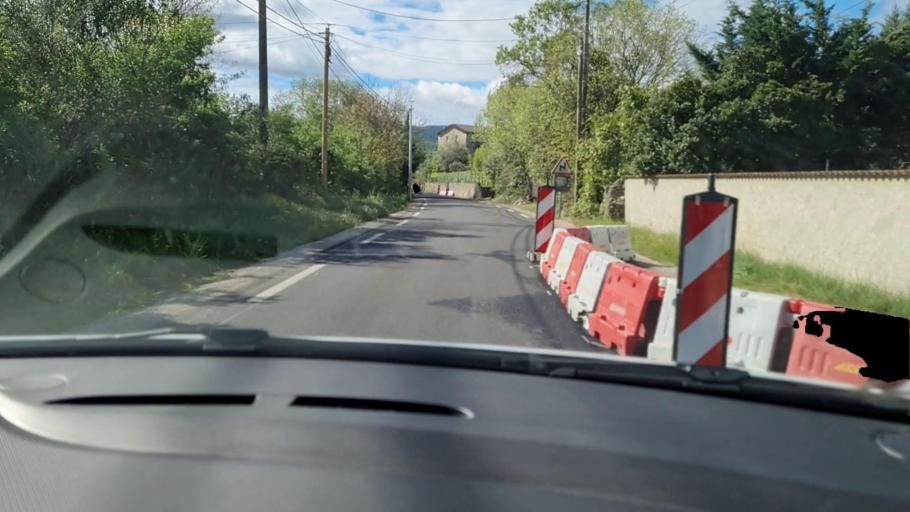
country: FR
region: Languedoc-Roussillon
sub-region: Departement du Gard
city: Sauve
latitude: 43.9495
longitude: 3.9480
